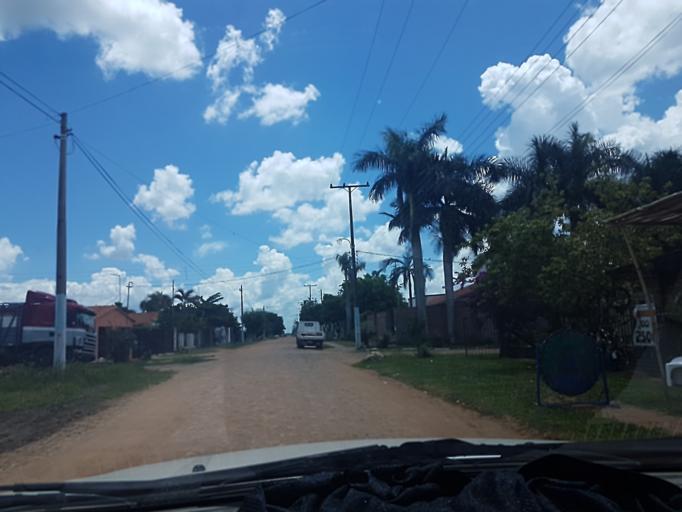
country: PY
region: Central
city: Limpio
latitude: -25.1374
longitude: -57.4807
